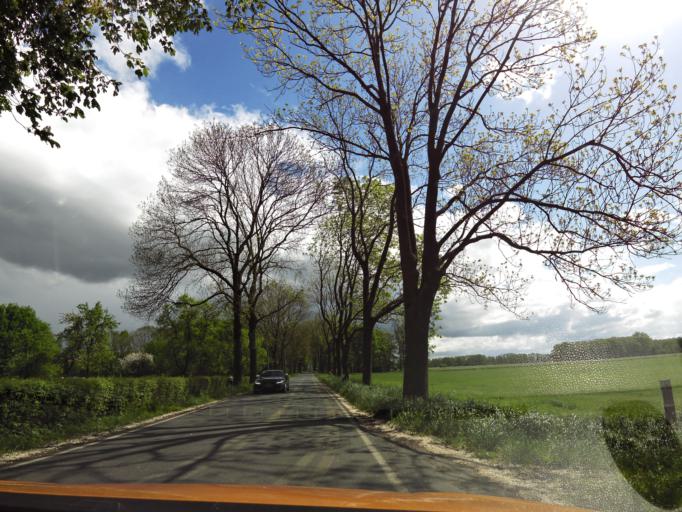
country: DE
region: Lower Saxony
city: Hude
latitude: 53.1605
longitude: 8.4076
